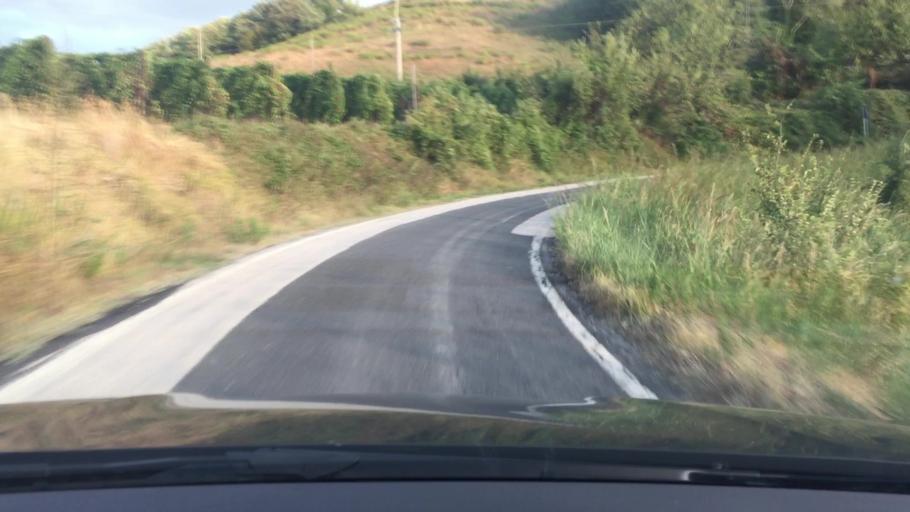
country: IT
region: Emilia-Romagna
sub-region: Provincia di Ravenna
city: Brisighella
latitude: 44.2070
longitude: 11.7779
